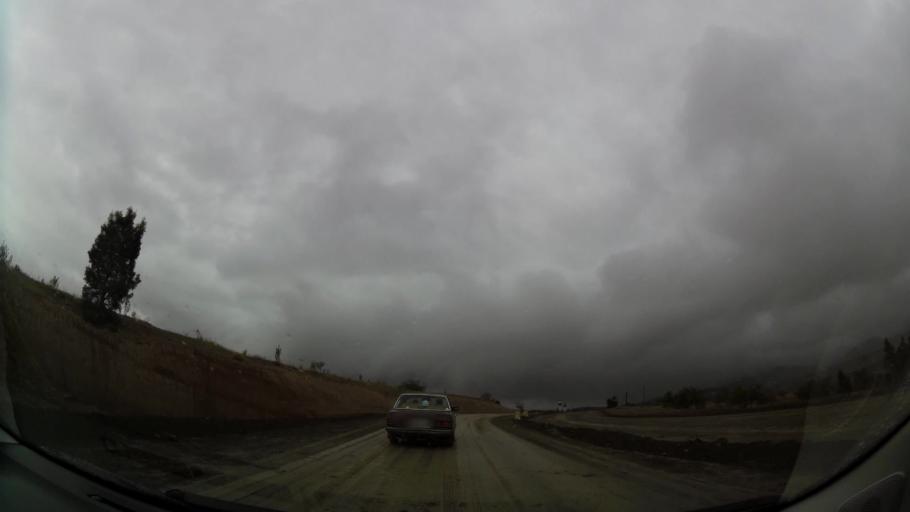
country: MA
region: Oriental
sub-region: Nador
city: Midar
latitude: 34.8965
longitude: -3.7726
